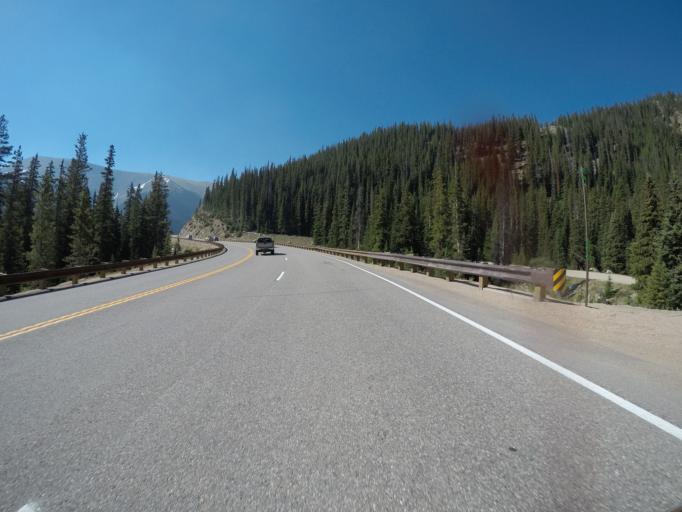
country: US
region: Colorado
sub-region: Grand County
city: Fraser
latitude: 39.8281
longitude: -105.7677
